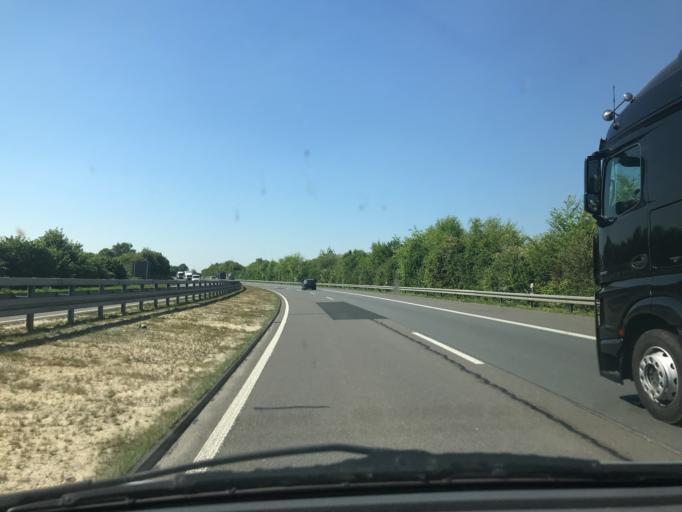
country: DE
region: North Rhine-Westphalia
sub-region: Regierungsbezirk Dusseldorf
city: Nettetal
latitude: 51.2928
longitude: 6.2637
